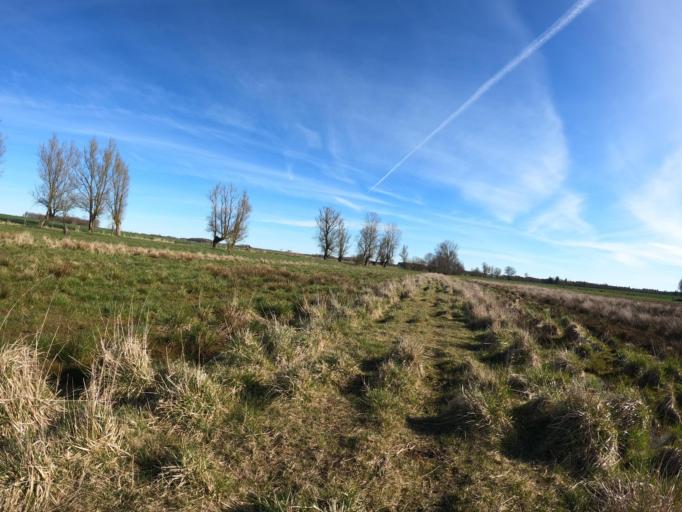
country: PL
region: West Pomeranian Voivodeship
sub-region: Powiat gryficki
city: Brojce
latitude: 53.9210
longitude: 15.3234
